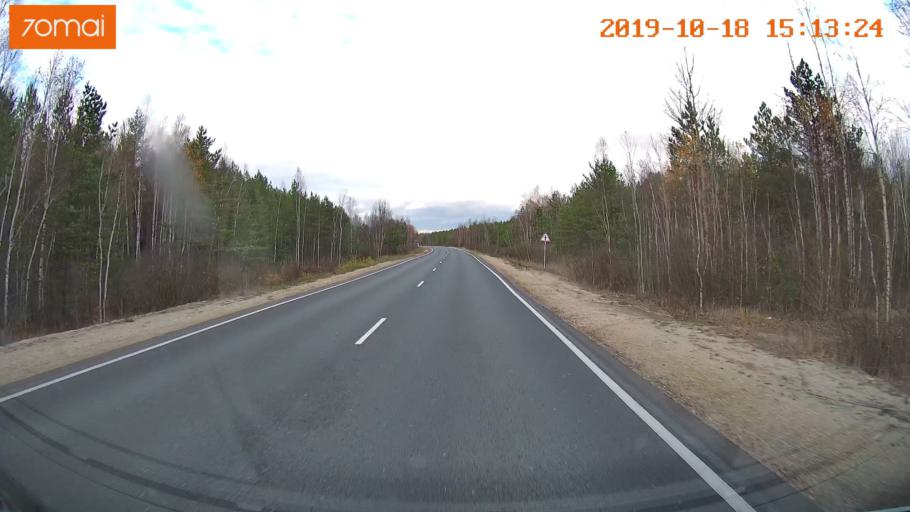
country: RU
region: Vladimir
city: Gus'-Khrustal'nyy
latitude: 55.5863
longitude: 40.7163
